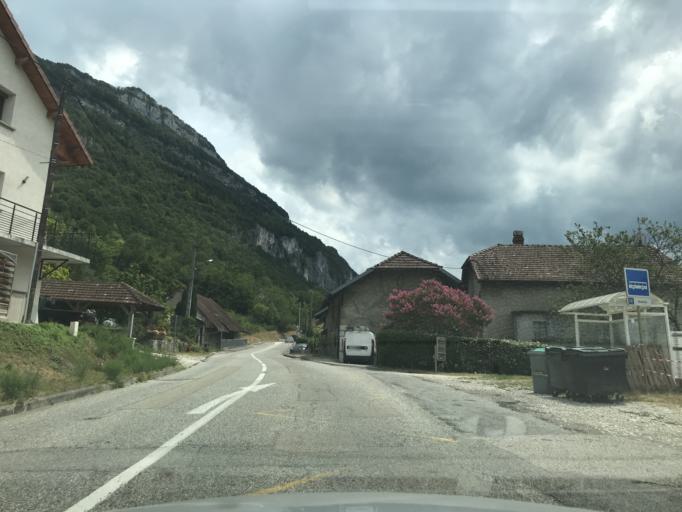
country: FR
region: Rhone-Alpes
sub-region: Departement de la Savoie
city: Chatillon
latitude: 45.7993
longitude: 5.8583
